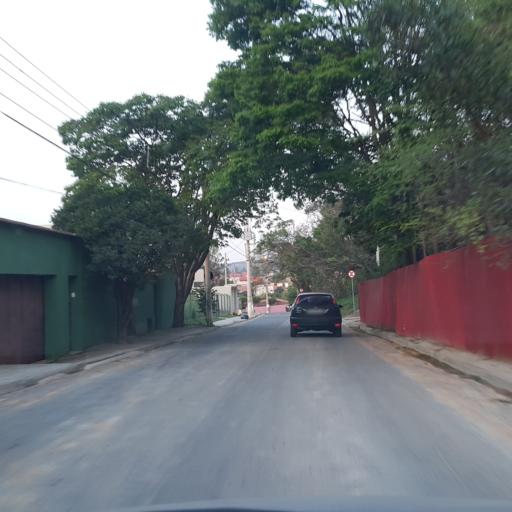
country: BR
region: Sao Paulo
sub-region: Vinhedo
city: Vinhedo
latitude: -23.0422
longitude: -46.9808
